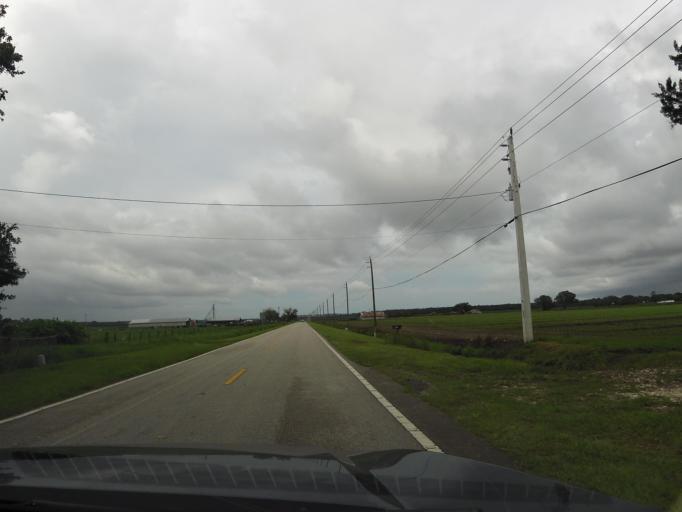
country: US
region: Florida
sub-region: Saint Johns County
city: Saint Augustine South
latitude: 29.8512
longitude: -81.5067
